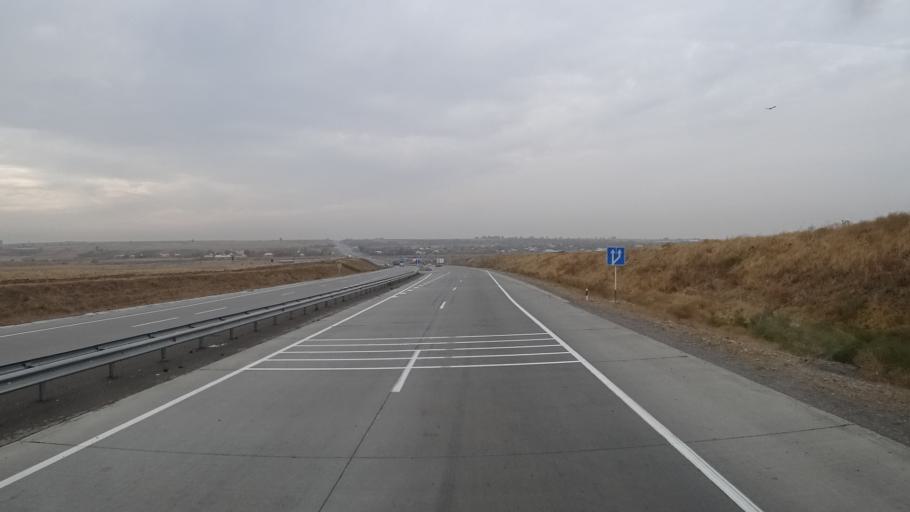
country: KZ
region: Ongtustik Qazaqstan
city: Aksu
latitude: 42.4641
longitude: 69.7706
